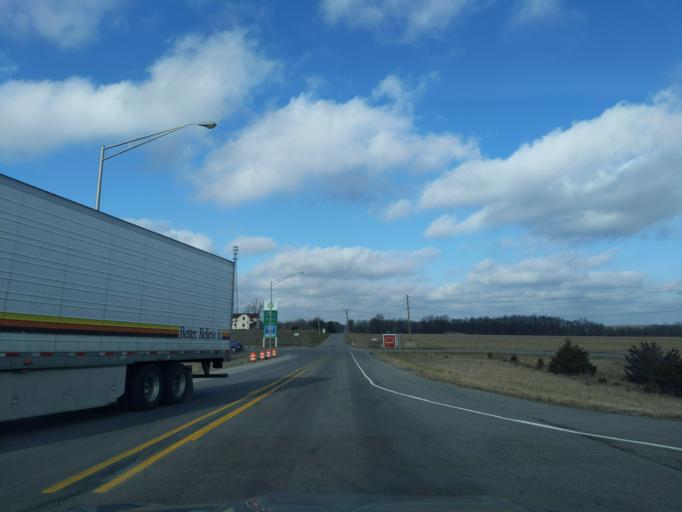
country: US
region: Indiana
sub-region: Ripley County
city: Batesville
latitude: 39.3179
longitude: -85.3258
